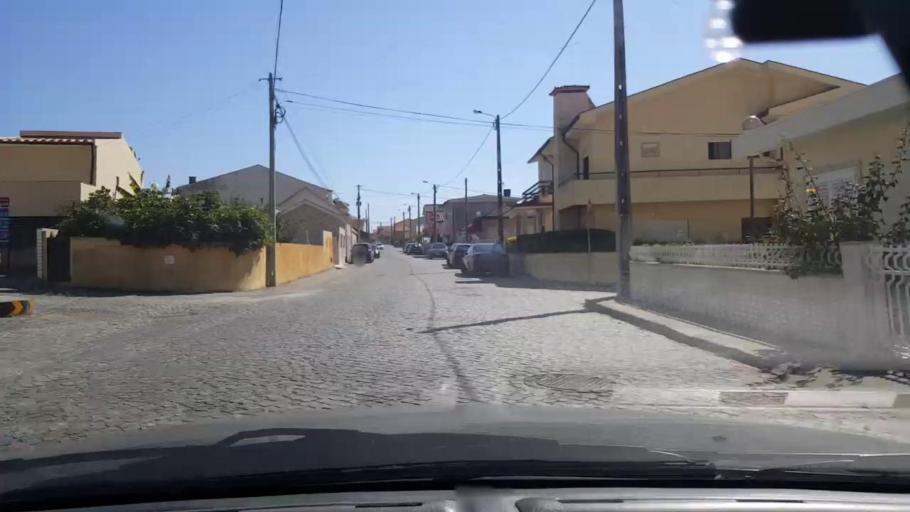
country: PT
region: Porto
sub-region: Matosinhos
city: Lavra
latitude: 41.2992
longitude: -8.7347
